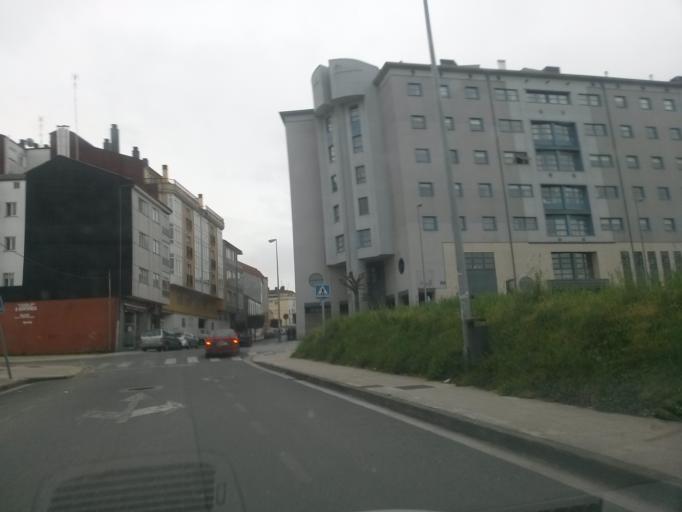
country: ES
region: Galicia
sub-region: Provincia de Lugo
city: Lugo
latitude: 43.0268
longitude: -7.5632
